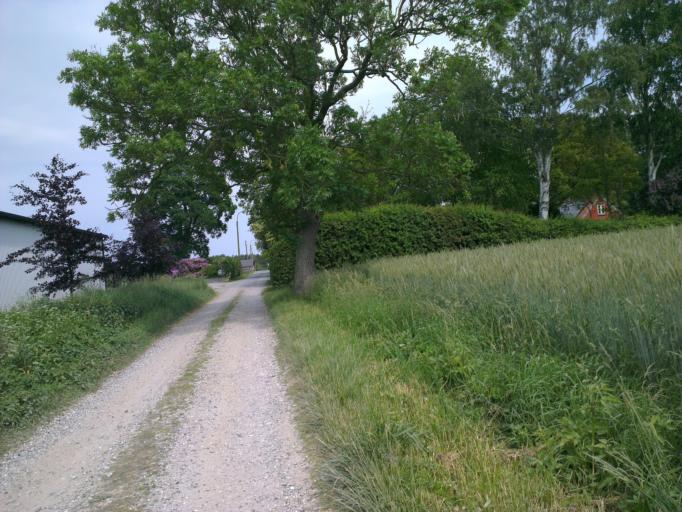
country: DK
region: Capital Region
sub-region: Frederikssund Kommune
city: Jaegerspris
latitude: 55.8159
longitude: 12.0077
